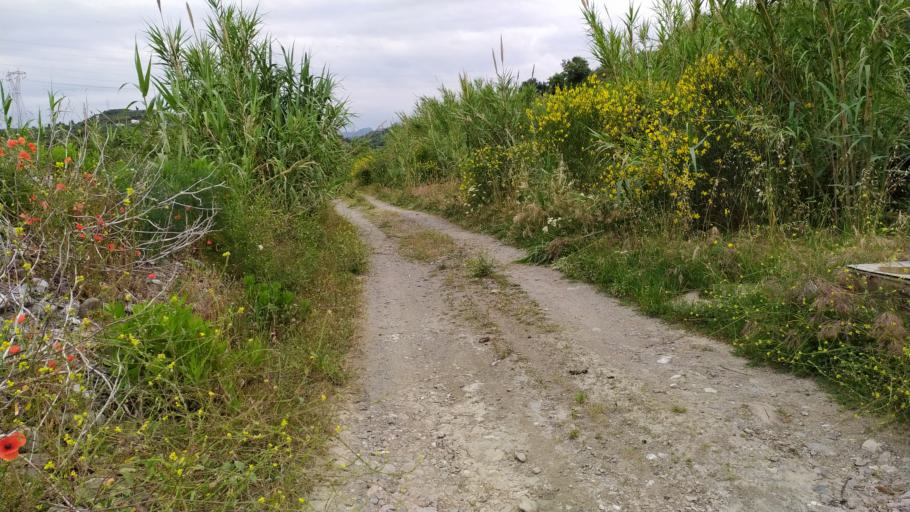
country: IT
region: Sicily
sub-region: Messina
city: San Filippo del Mela
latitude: 38.1718
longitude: 15.2788
